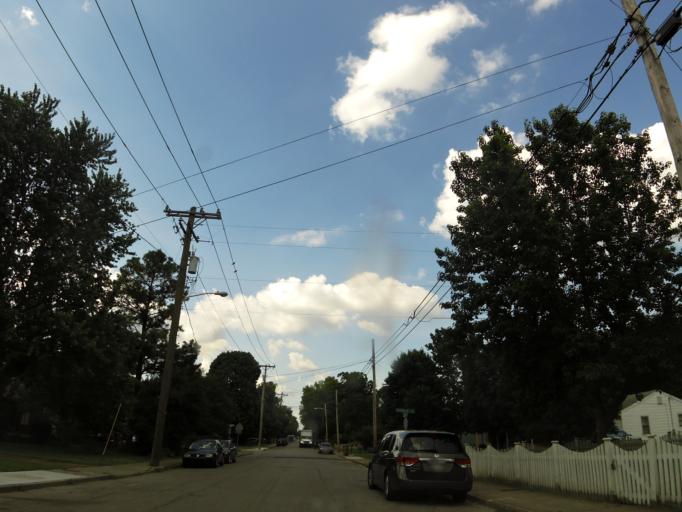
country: US
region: Tennessee
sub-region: Davidson County
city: Nashville
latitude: 36.1835
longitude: -86.7344
